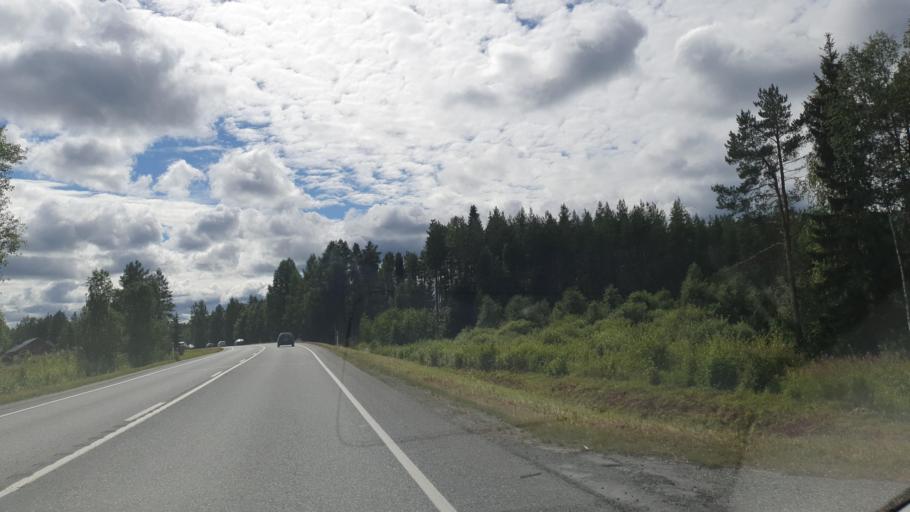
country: FI
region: Kainuu
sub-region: Kajaani
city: Kajaani
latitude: 64.1473
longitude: 27.5038
